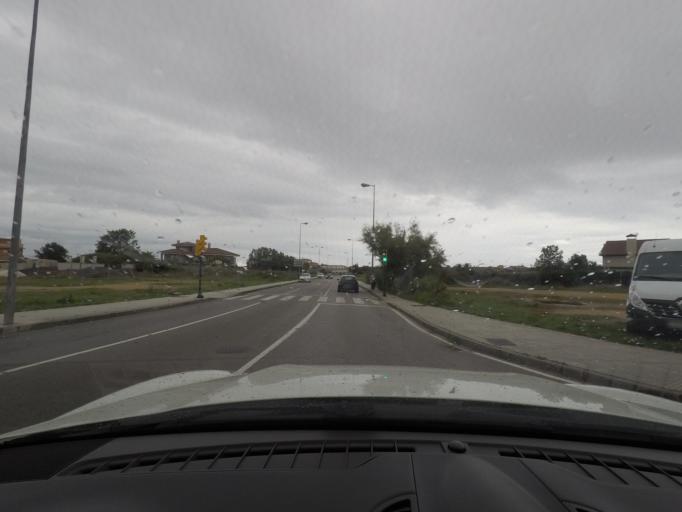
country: ES
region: Asturias
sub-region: Province of Asturias
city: Gijon
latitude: 43.5420
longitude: -5.6420
